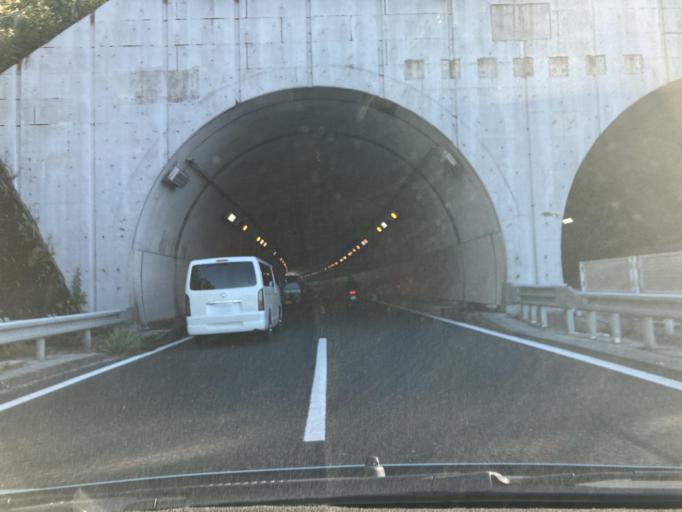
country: JP
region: Okinawa
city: Chatan
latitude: 26.3089
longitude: 127.7884
